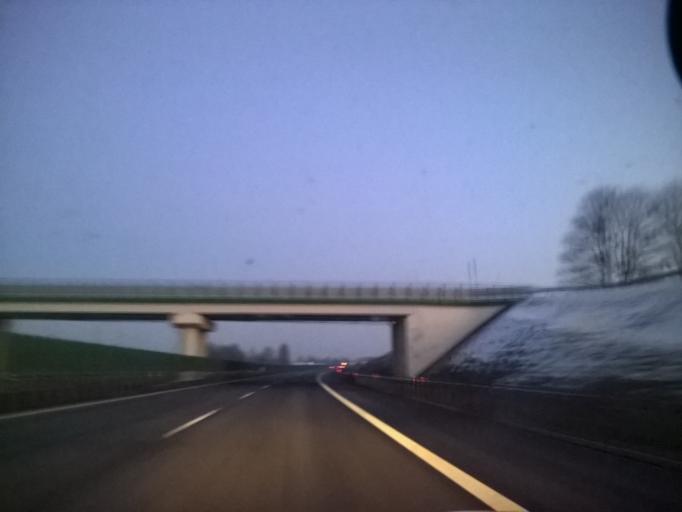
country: PL
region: Warmian-Masurian Voivodeship
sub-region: Powiat olsztynski
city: Biskupiec
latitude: 53.8392
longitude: 21.0159
